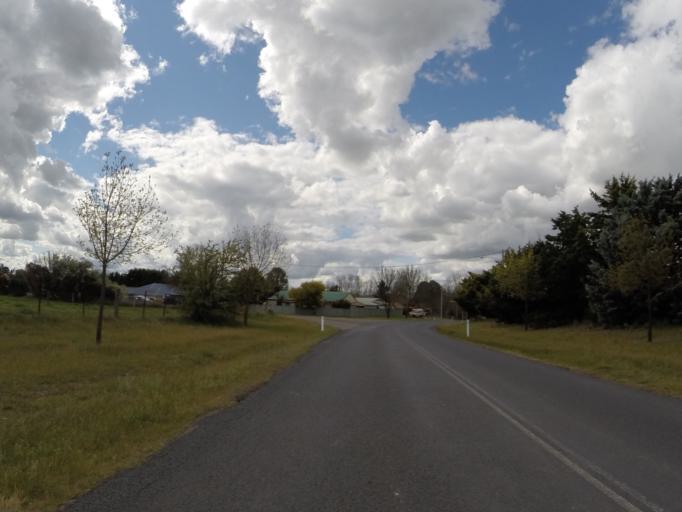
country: AU
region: New South Wales
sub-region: Yass Valley
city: Yass
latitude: -34.8598
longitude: 148.9166
